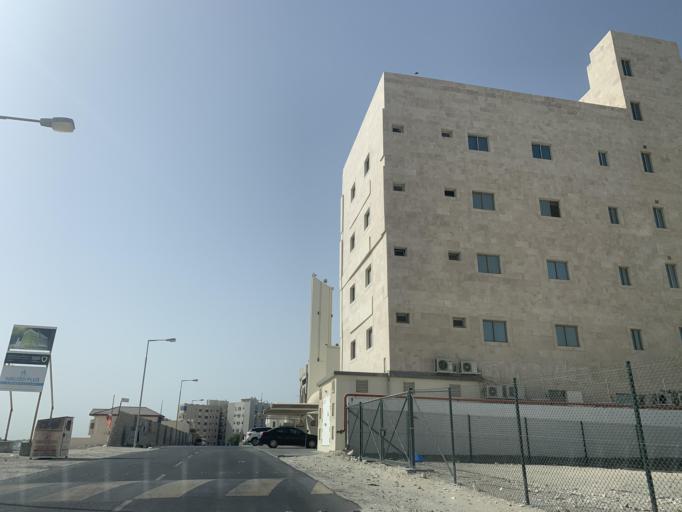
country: BH
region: Northern
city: Ar Rifa'
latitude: 26.1503
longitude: 50.5683
